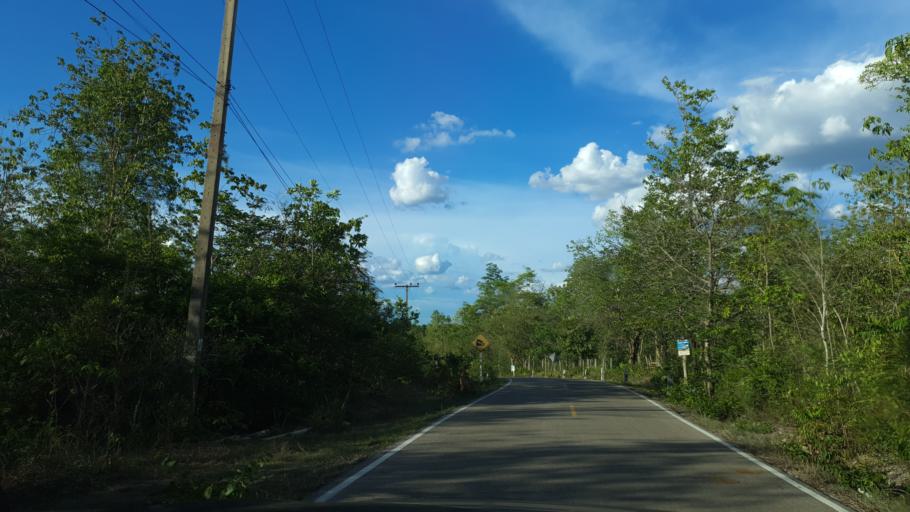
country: TH
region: Lampang
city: Sop Prap
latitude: 17.8782
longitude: 99.3092
